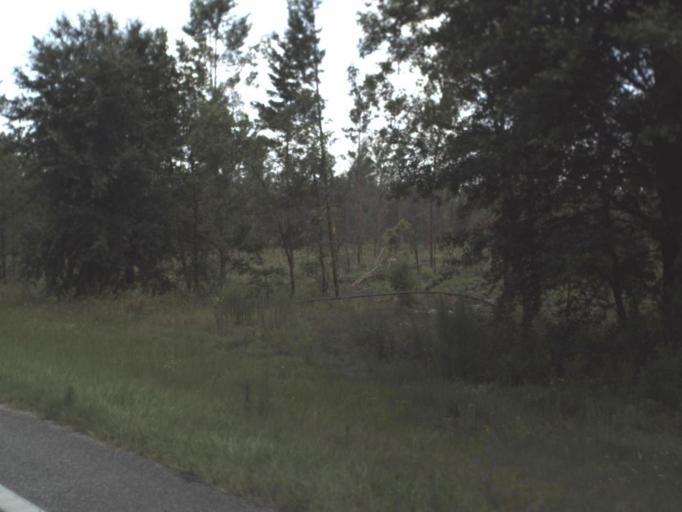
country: US
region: Florida
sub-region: Madison County
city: Madison
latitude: 30.4017
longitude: -83.2179
